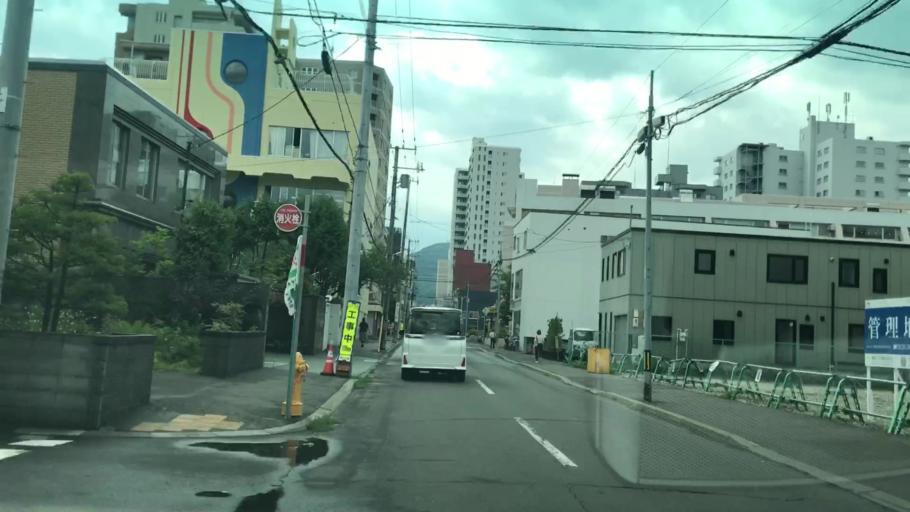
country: JP
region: Hokkaido
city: Sapporo
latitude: 43.0597
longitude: 141.3209
